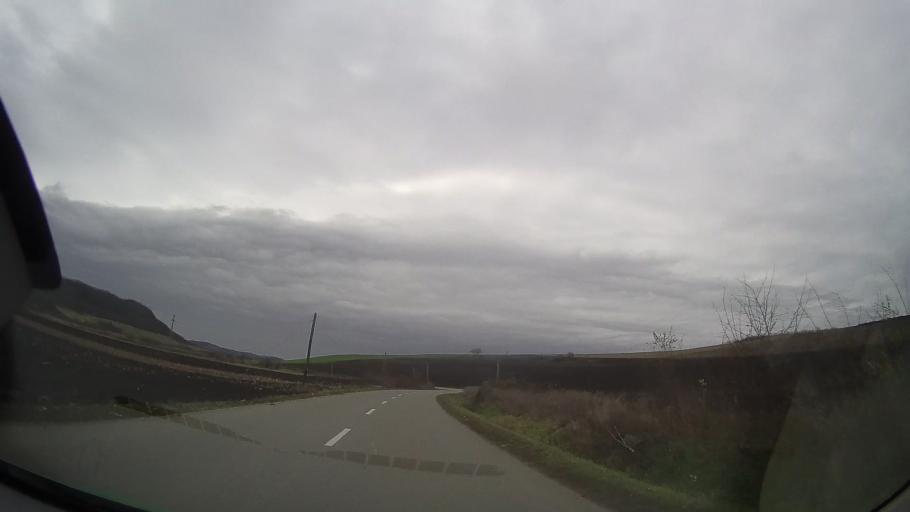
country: RO
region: Bistrita-Nasaud
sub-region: Comuna Milas
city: Milas
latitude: 46.8046
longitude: 24.4280
